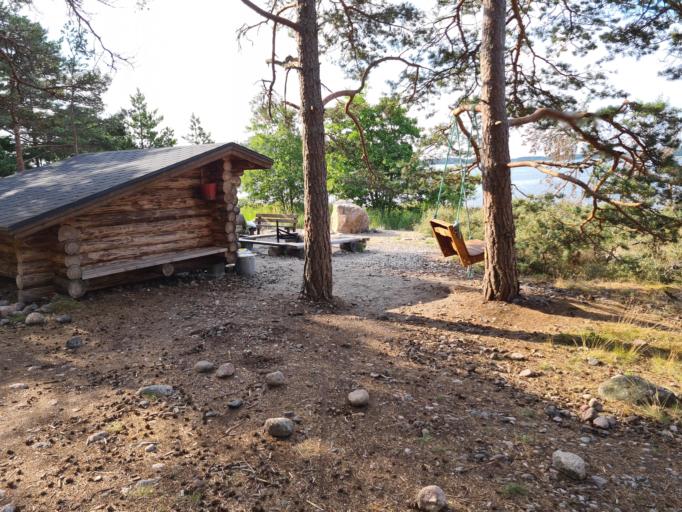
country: FI
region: Varsinais-Suomi
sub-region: Vakka-Suomi
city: Pyhaeranta
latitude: 61.0324
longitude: 21.3300
